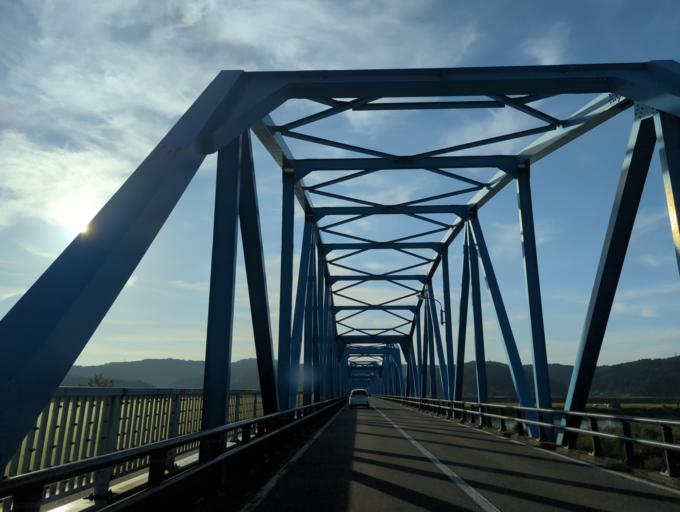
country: JP
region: Niigata
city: Nagaoka
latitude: 37.5534
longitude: 138.8240
